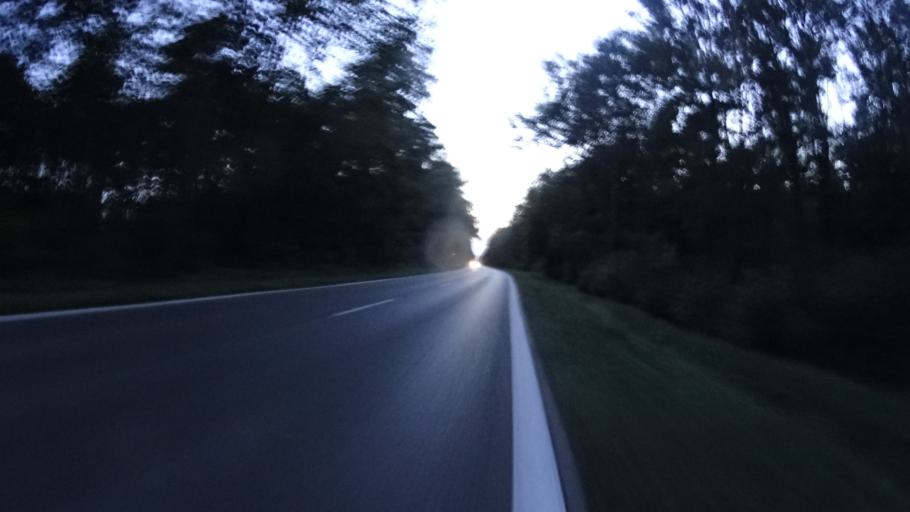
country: PL
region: Masovian Voivodeship
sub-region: Powiat warszawski zachodni
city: Leszno
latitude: 52.2634
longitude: 20.6610
